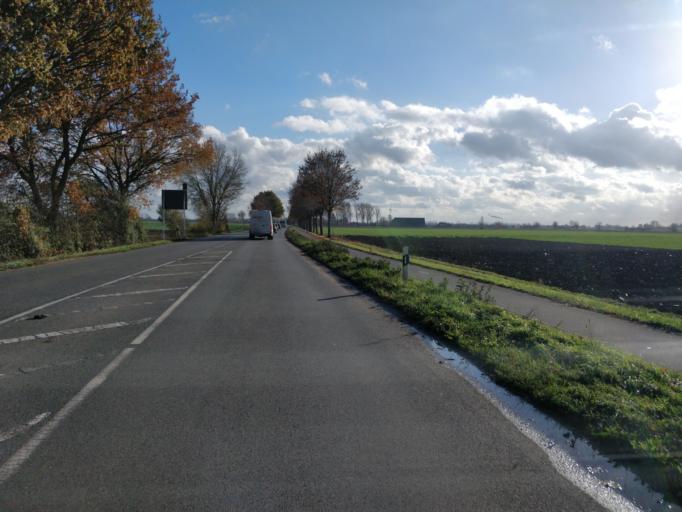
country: DE
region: North Rhine-Westphalia
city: Rees
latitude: 51.7966
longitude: 6.3711
